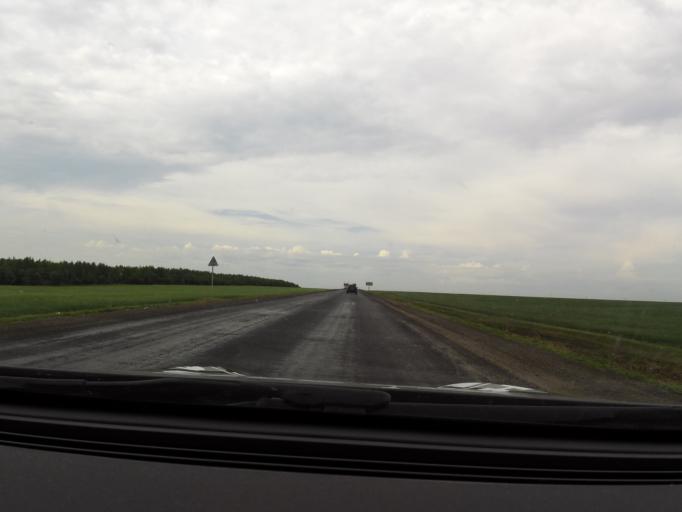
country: RU
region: Bashkortostan
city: Iglino
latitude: 54.7555
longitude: 56.3578
